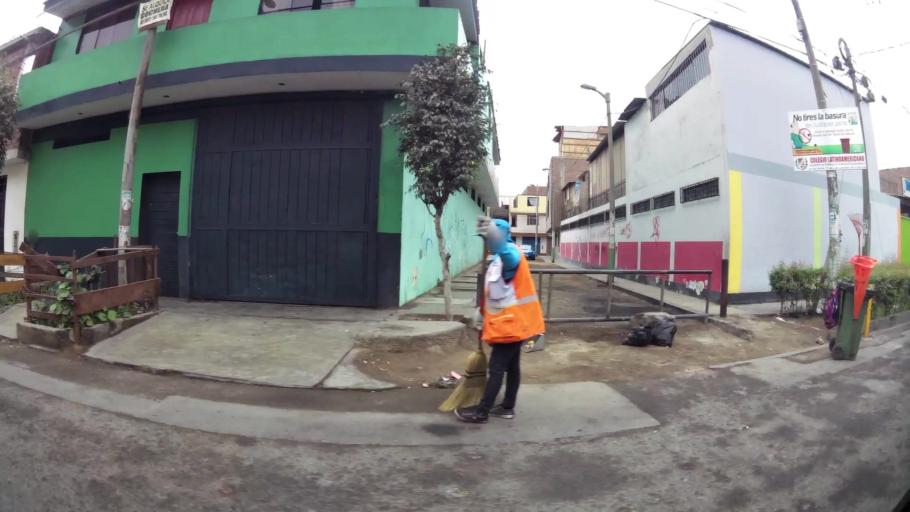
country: PE
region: Lima
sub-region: Lima
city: Independencia
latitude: -11.9743
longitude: -77.0751
